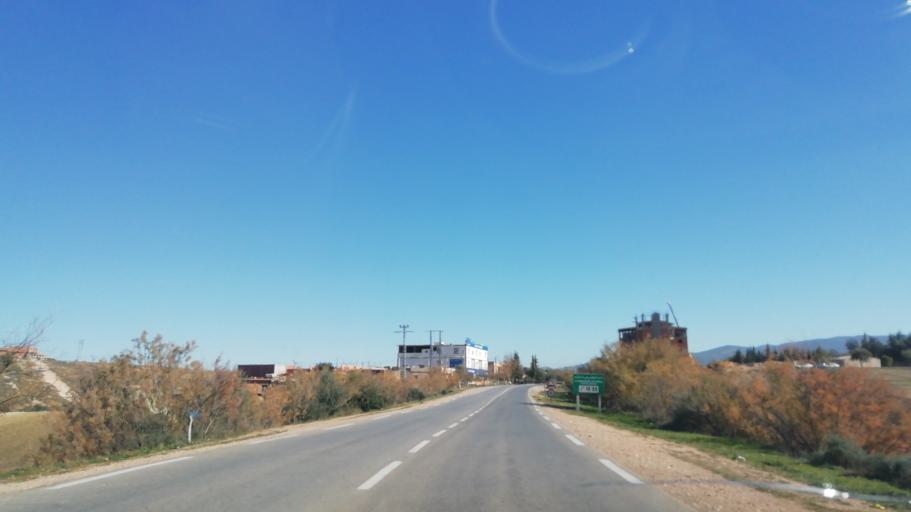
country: DZ
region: Tlemcen
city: Beni Mester
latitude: 34.8257
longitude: -1.5624
